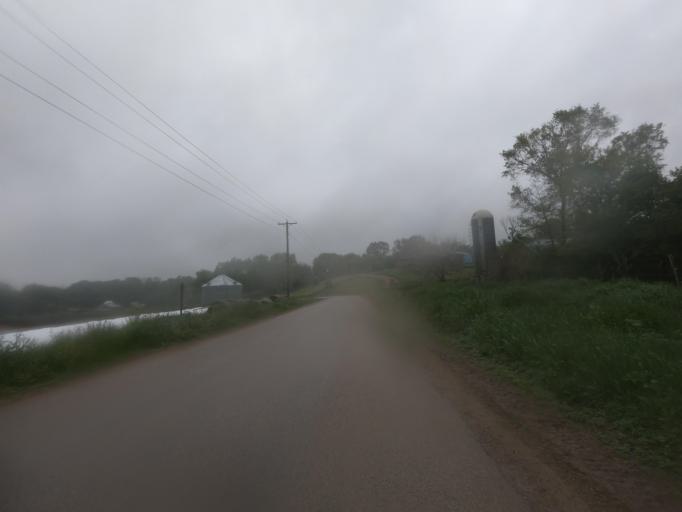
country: US
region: Wisconsin
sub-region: Grant County
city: Hazel Green
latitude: 42.5094
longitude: -90.4830
